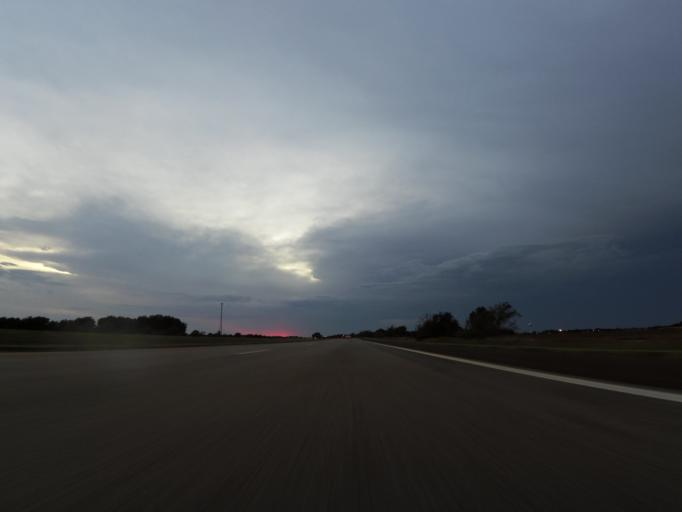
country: US
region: Kansas
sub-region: Reno County
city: Haven
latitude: 37.8933
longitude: -97.7626
